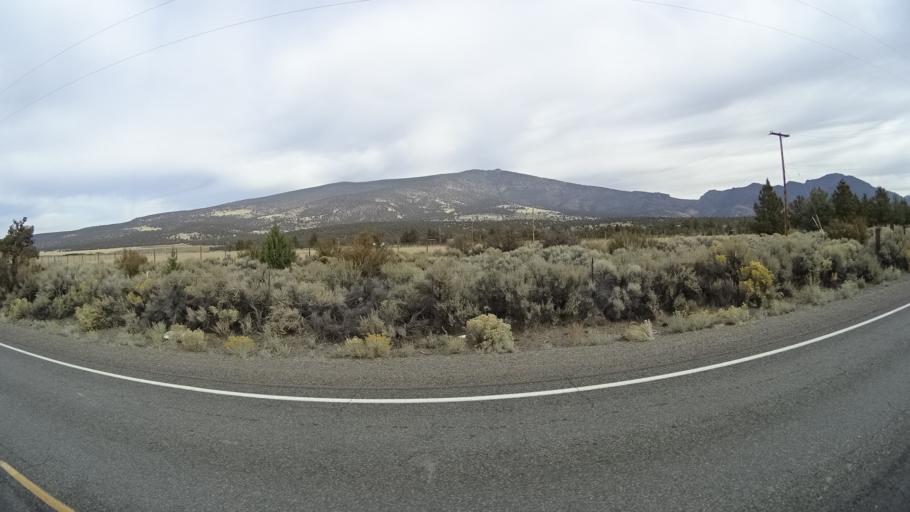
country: US
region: California
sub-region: Siskiyou County
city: Weed
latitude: 41.5837
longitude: -122.2941
